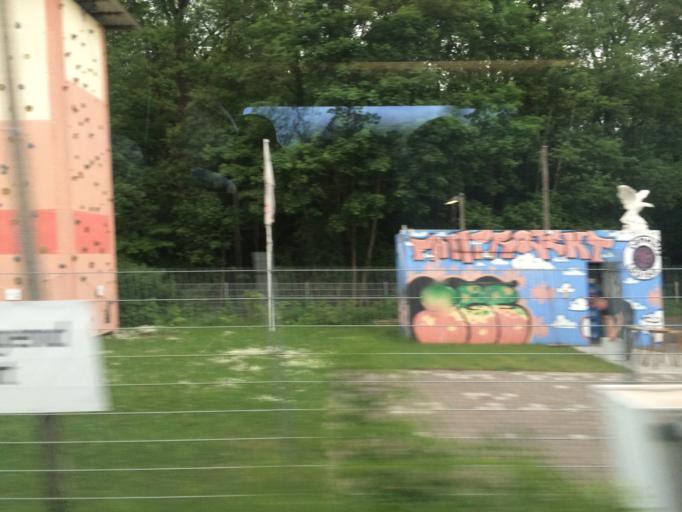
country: DE
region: Hesse
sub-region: Regierungsbezirk Darmstadt
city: Frankfurt am Main
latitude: 50.0838
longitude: 8.6702
